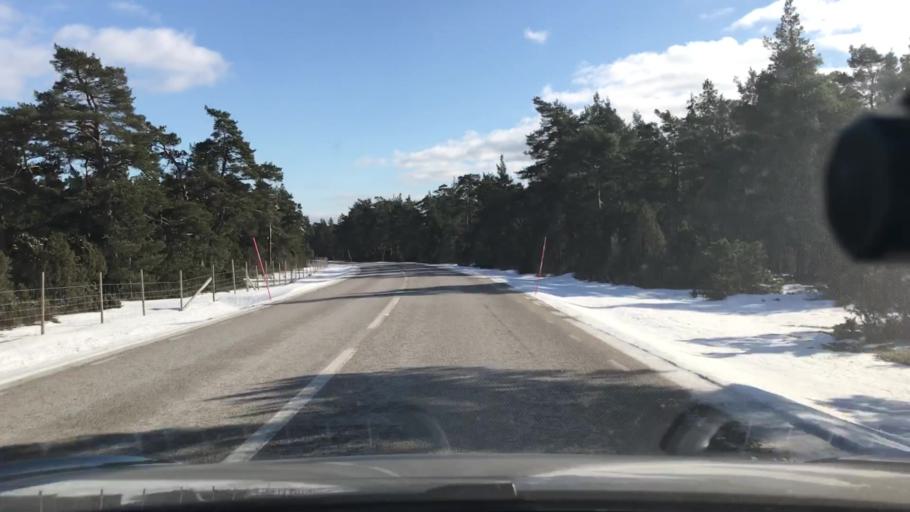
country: SE
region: Gotland
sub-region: Gotland
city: Hemse
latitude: 57.3506
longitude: 18.6881
